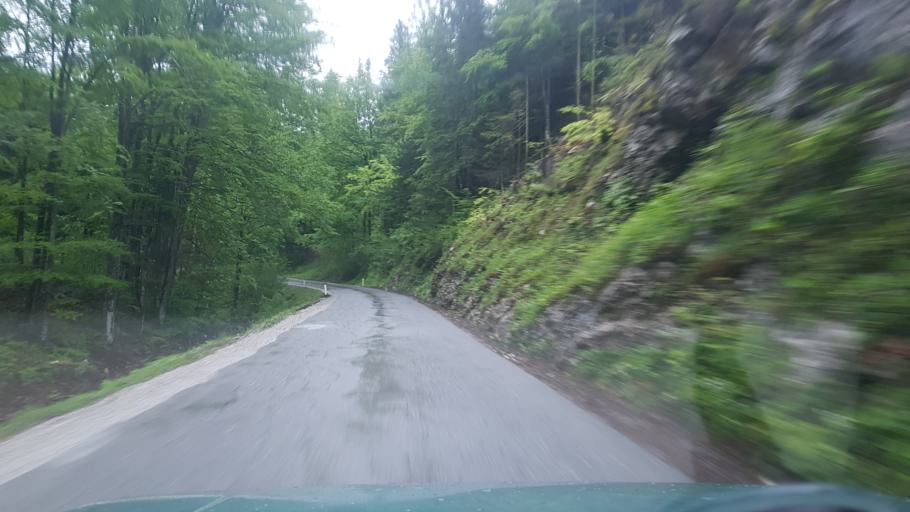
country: SI
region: Bohinj
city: Bohinjska Bistrica
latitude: 46.2756
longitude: 14.0129
